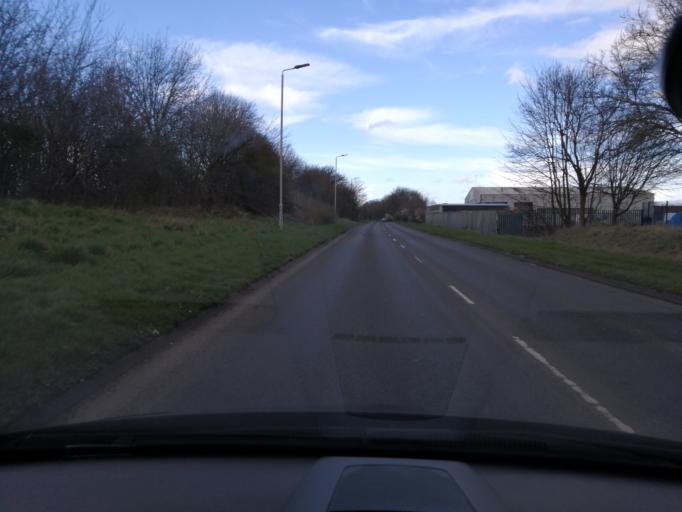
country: GB
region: England
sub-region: Peterborough
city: Peterborough
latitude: 52.5857
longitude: -0.2658
